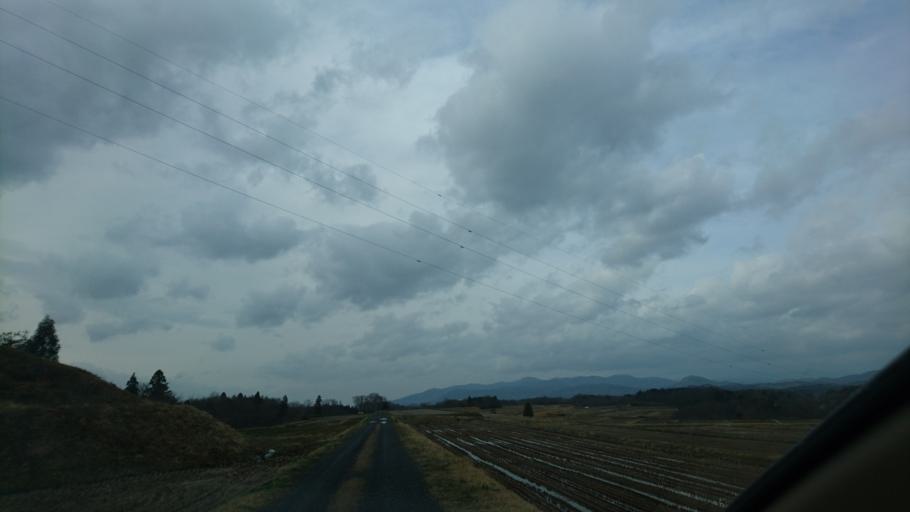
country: JP
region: Iwate
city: Ichinoseki
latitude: 38.8847
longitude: 141.1610
